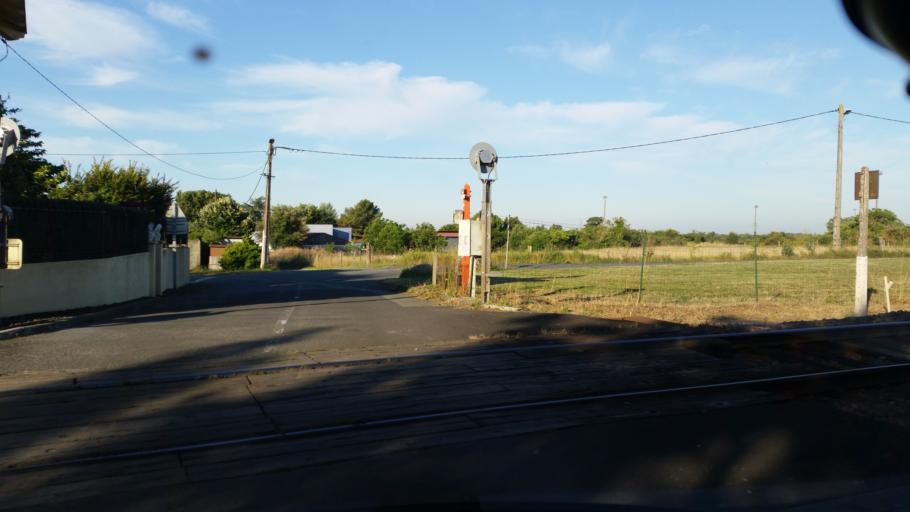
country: FR
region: Poitou-Charentes
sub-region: Departement de la Charente-Maritime
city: Marans
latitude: 46.3019
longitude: -0.9948
